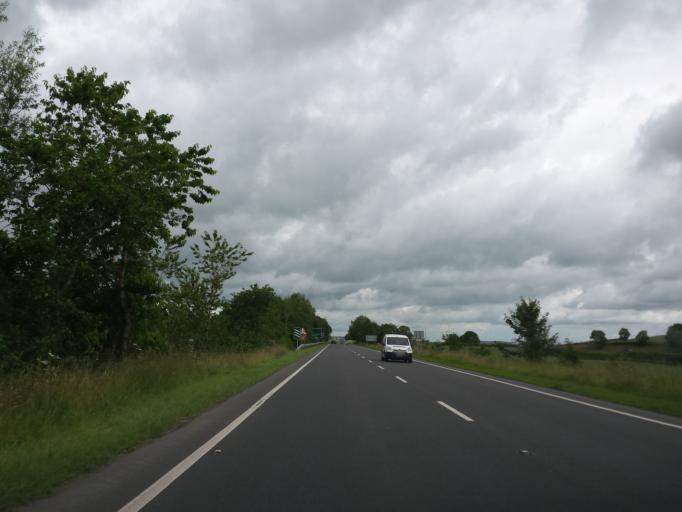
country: GB
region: Scotland
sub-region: Dumfries and Galloway
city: Castle Douglas
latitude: 54.9553
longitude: -3.9228
